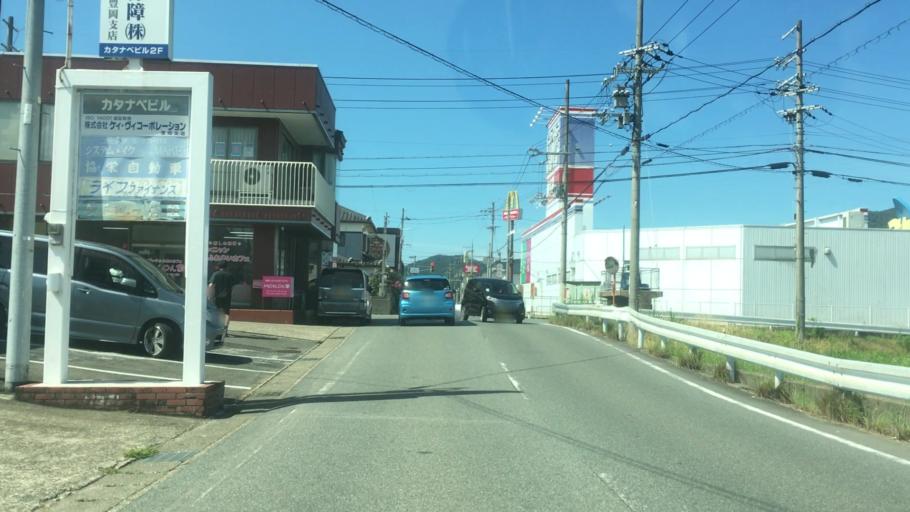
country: JP
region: Hyogo
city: Toyooka
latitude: 35.5533
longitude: 134.8130
